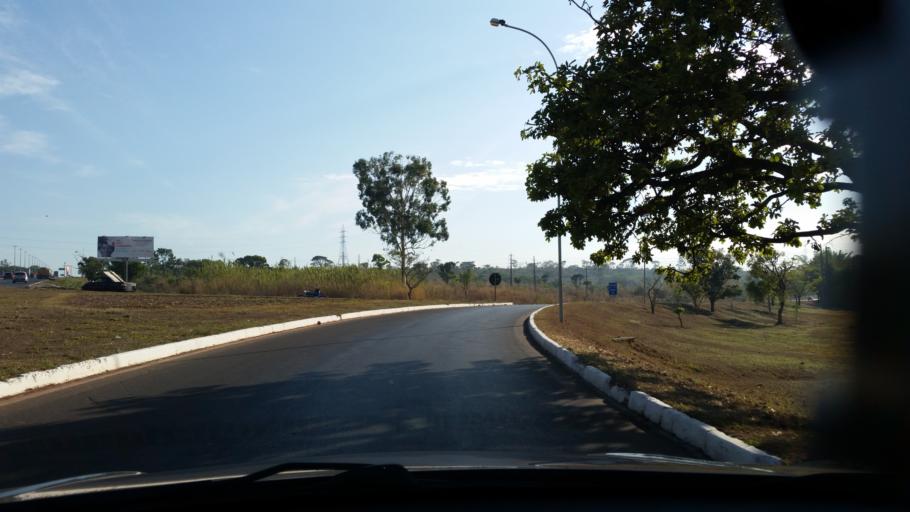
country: BR
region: Federal District
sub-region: Brasilia
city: Brasilia
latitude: -15.7248
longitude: -47.9070
